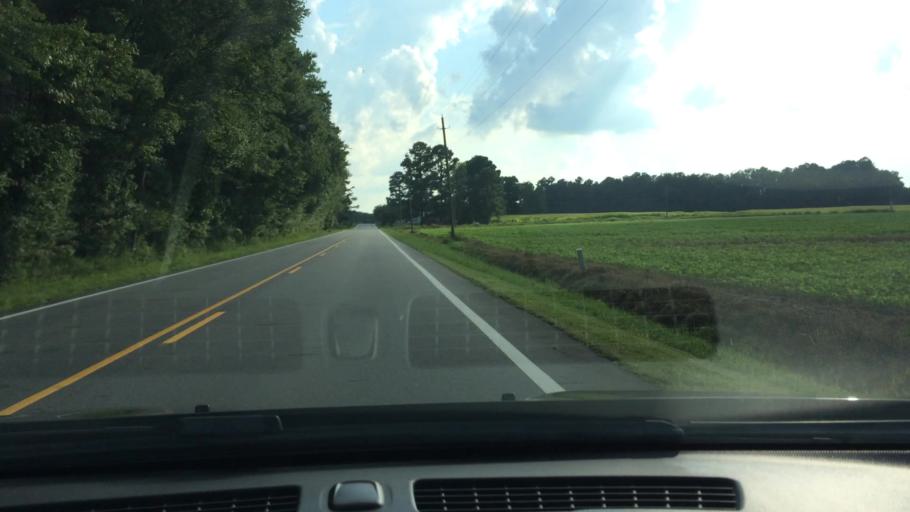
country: US
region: North Carolina
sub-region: Craven County
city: Vanceboro
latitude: 35.4231
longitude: -77.2245
